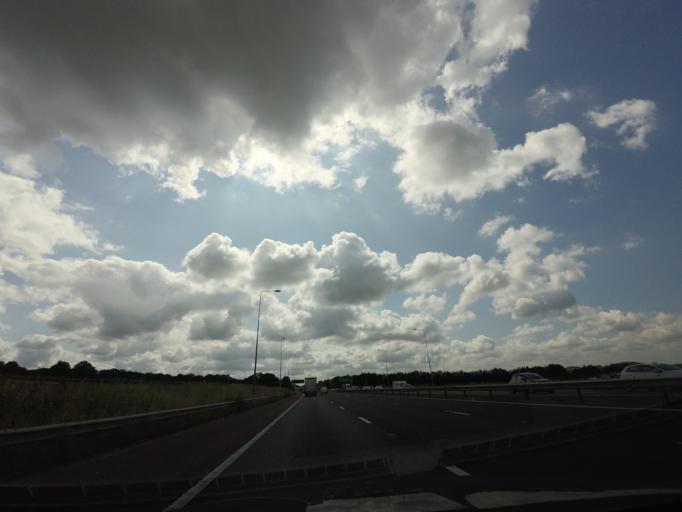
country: GB
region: England
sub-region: Lancashire
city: Euxton
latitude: 53.6394
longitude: -2.6923
